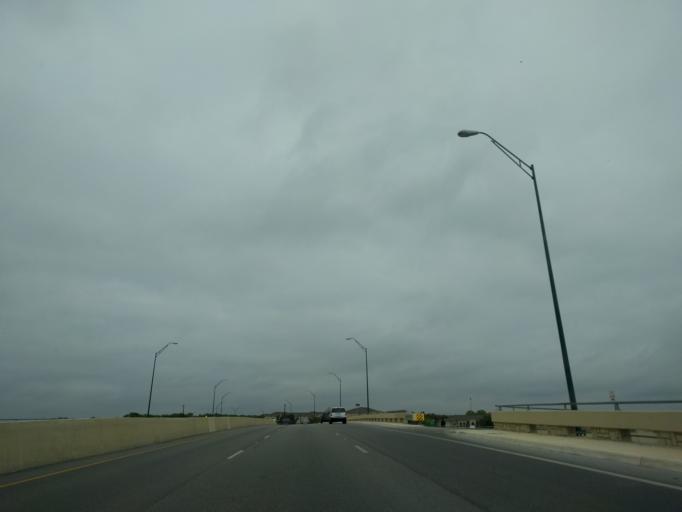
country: US
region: Texas
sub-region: Bexar County
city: Castle Hills
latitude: 29.5608
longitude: -98.5060
